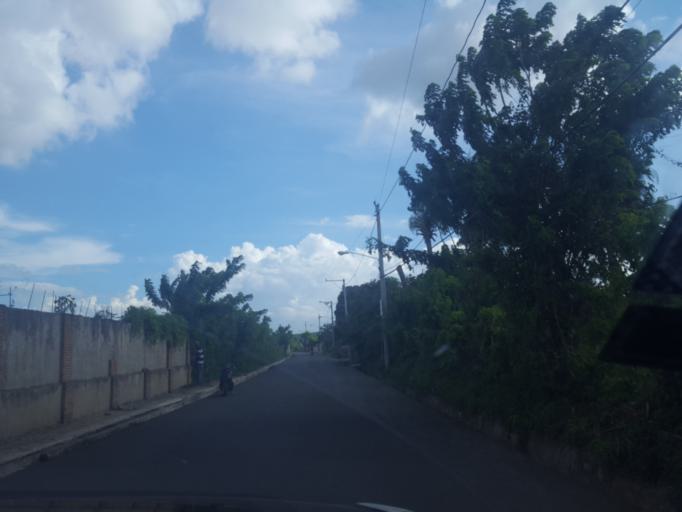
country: DO
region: Santiago
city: Licey al Medio
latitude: 19.3808
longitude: -70.6220
